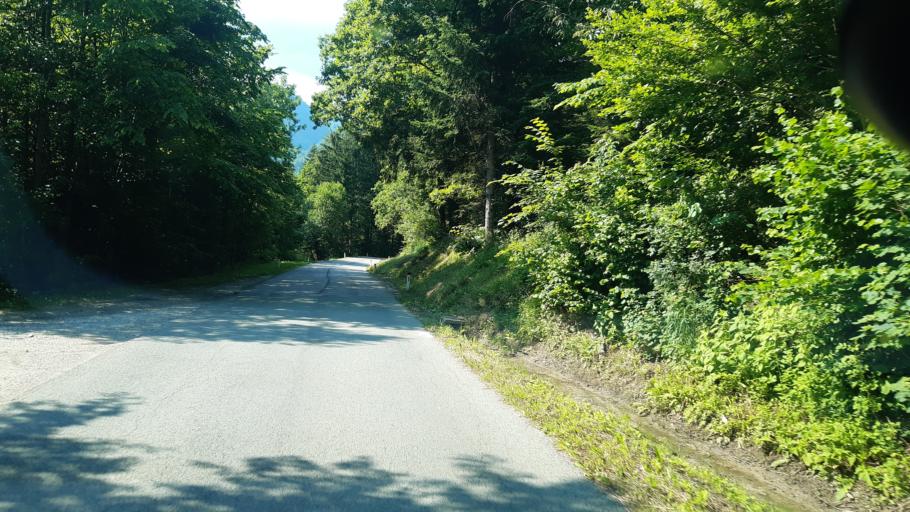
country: SI
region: Radovljica
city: Radovljica
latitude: 46.3738
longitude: 14.2173
